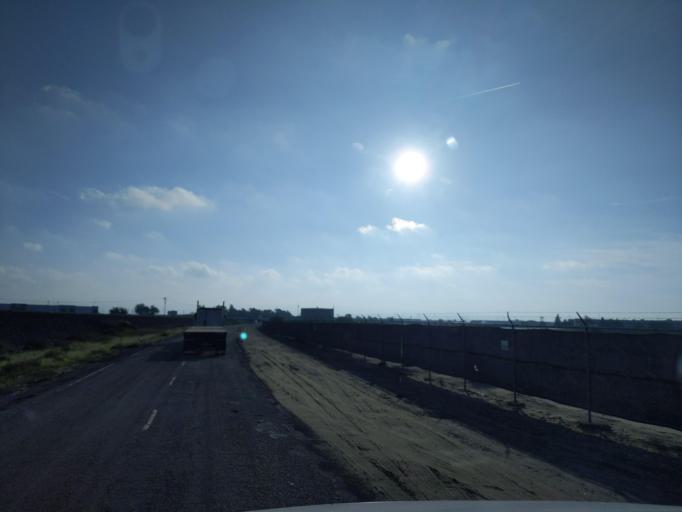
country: US
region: California
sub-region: San Joaquin County
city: Lathrop
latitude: 37.8004
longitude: -121.2776
